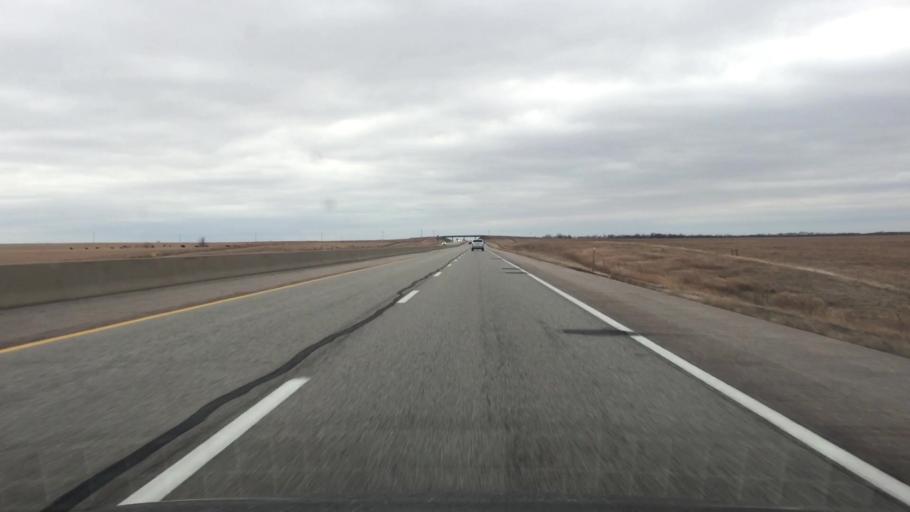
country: US
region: Kansas
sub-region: Butler County
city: El Dorado
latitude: 37.9924
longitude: -96.6992
